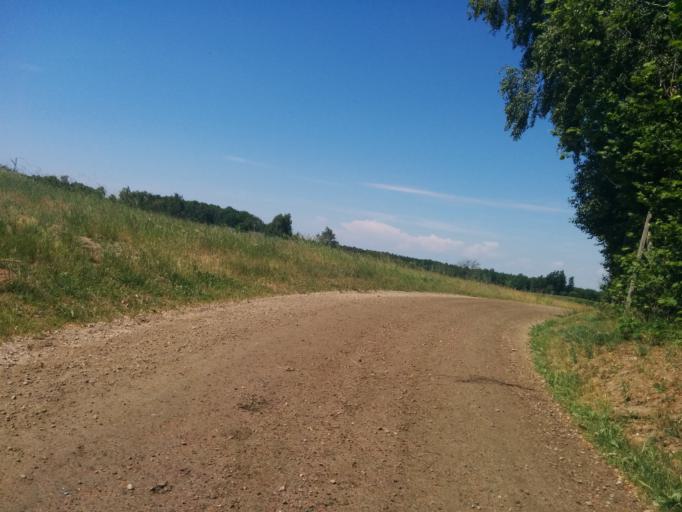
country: SE
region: Skane
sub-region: Lunds Kommun
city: Genarp
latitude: 55.5894
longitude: 13.3811
